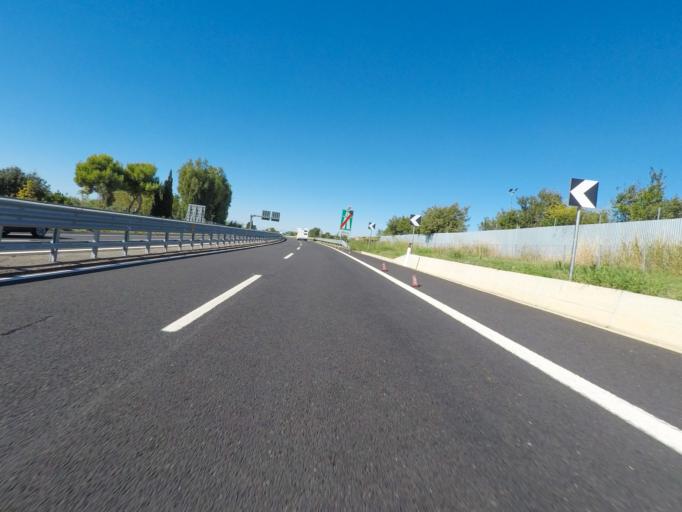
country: IT
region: Latium
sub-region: Provincia di Viterbo
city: Tarquinia
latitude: 42.2676
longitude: 11.7198
